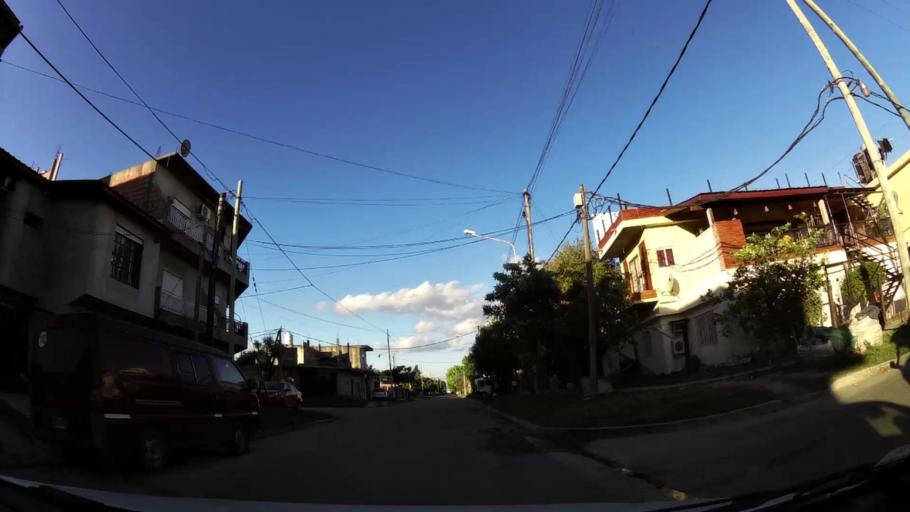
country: AR
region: Buenos Aires
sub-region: Partido de Moron
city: Moron
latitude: -34.7123
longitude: -58.6174
